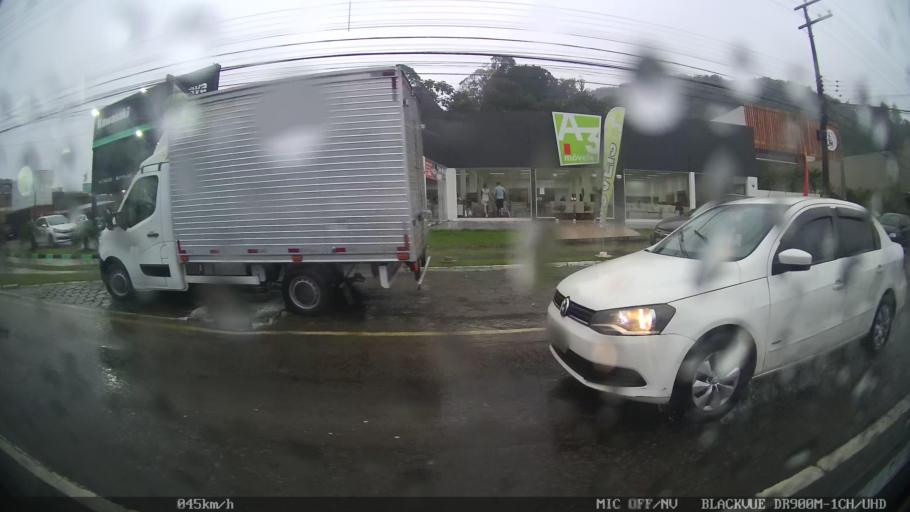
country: BR
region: Santa Catarina
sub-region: Balneario Camboriu
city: Balneario Camboriu
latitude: -26.9487
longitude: -48.6405
